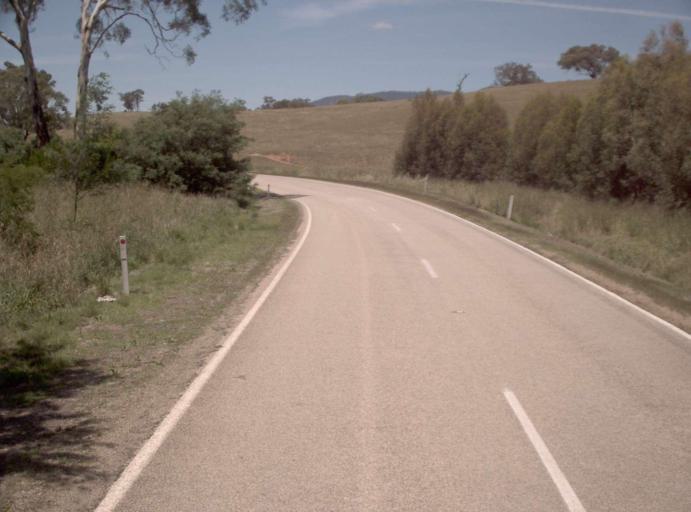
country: AU
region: Victoria
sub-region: East Gippsland
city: Bairnsdale
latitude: -37.2938
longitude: 147.7449
